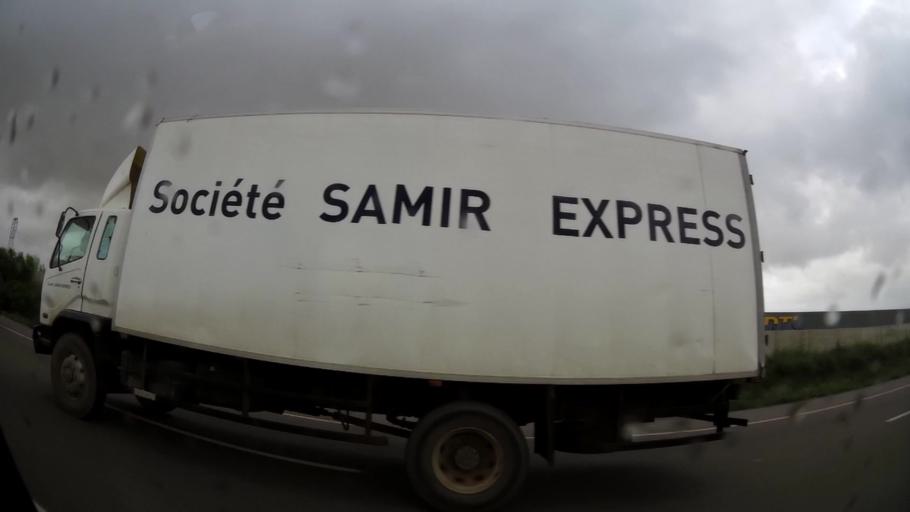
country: MA
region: Grand Casablanca
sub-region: Mohammedia
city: Mohammedia
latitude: 33.6554
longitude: -7.4120
